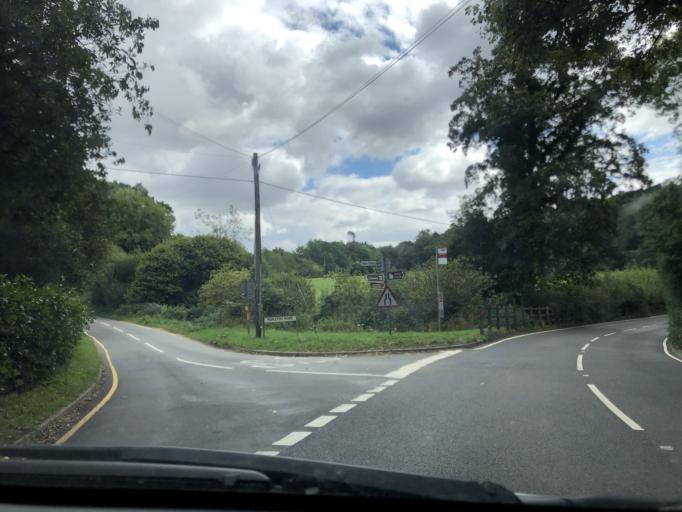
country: GB
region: England
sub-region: Kent
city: Westerham
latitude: 51.2507
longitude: 0.0780
